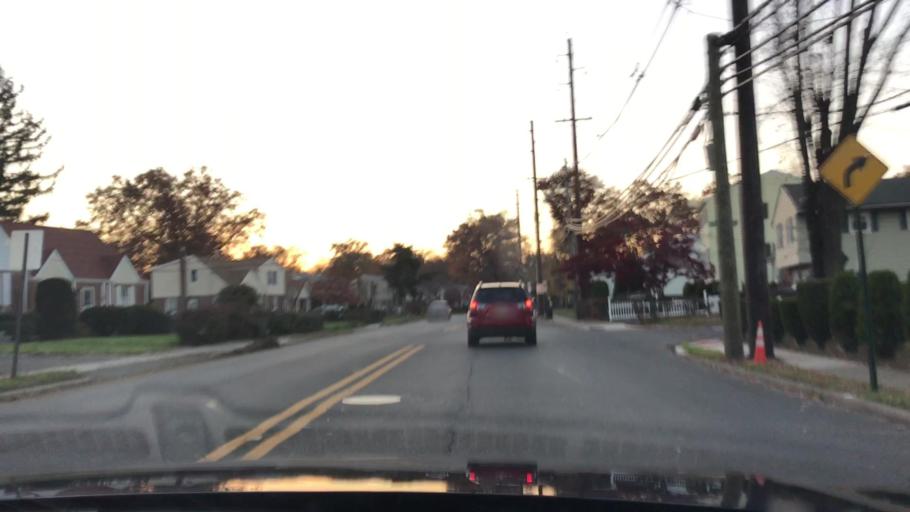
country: US
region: New Jersey
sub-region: Bergen County
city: Bergenfield
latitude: 40.9140
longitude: -74.0036
